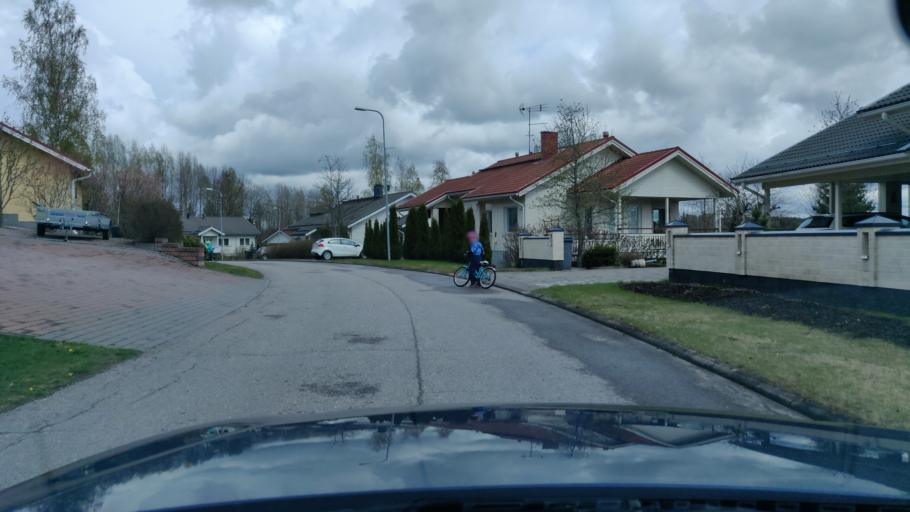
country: FI
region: Uusimaa
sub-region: Helsinki
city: Nurmijaervi
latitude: 60.3626
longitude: 24.7329
